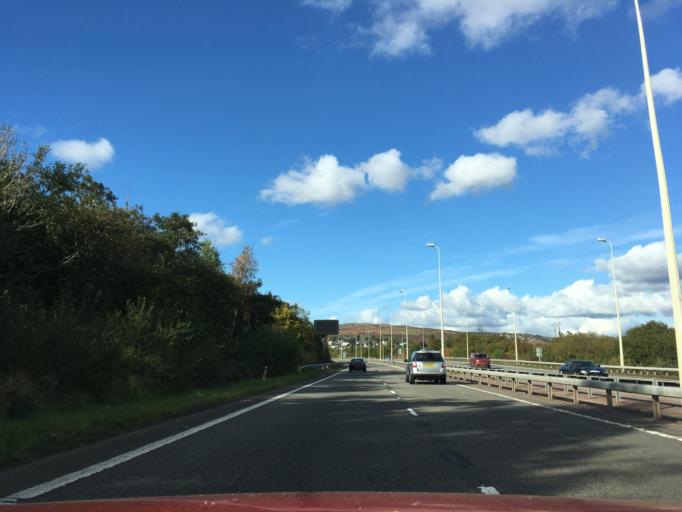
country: GB
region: Wales
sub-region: Merthyr Tydfil County Borough
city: Merthyr Tydfil
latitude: 51.7523
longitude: -3.3983
